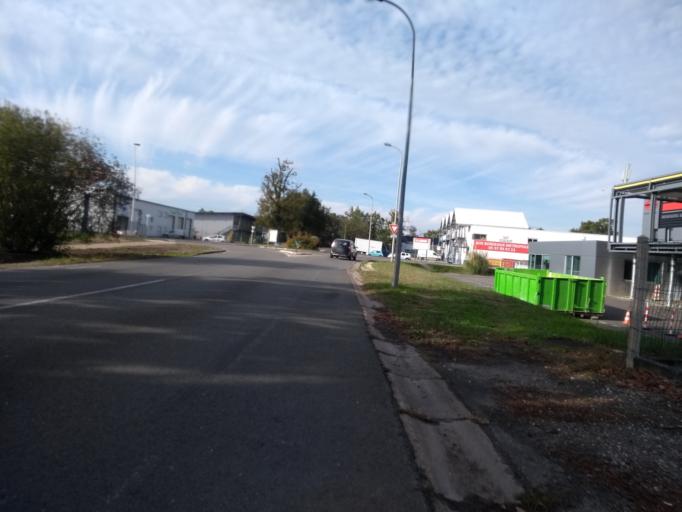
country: FR
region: Aquitaine
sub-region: Departement de la Gironde
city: Canejan
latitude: 44.7746
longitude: -0.6638
